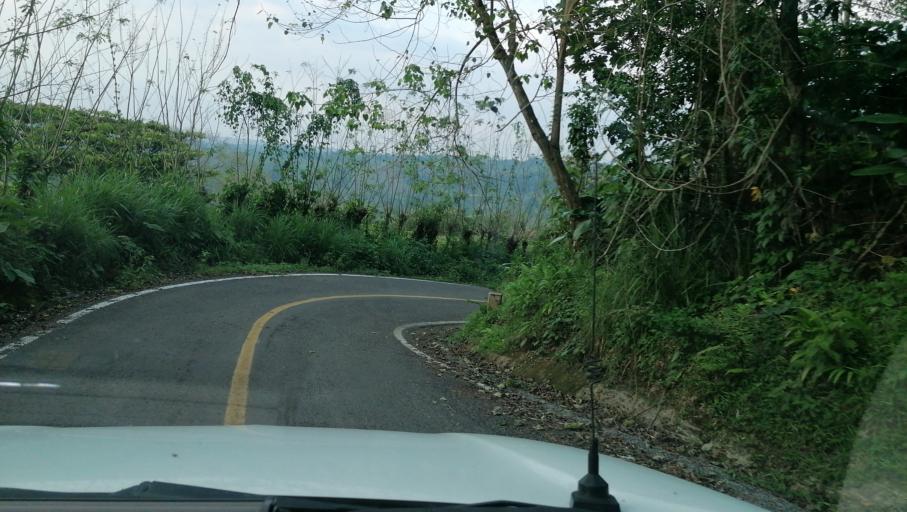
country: MX
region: Chiapas
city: Pichucalco
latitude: 17.5106
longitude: -93.2109
